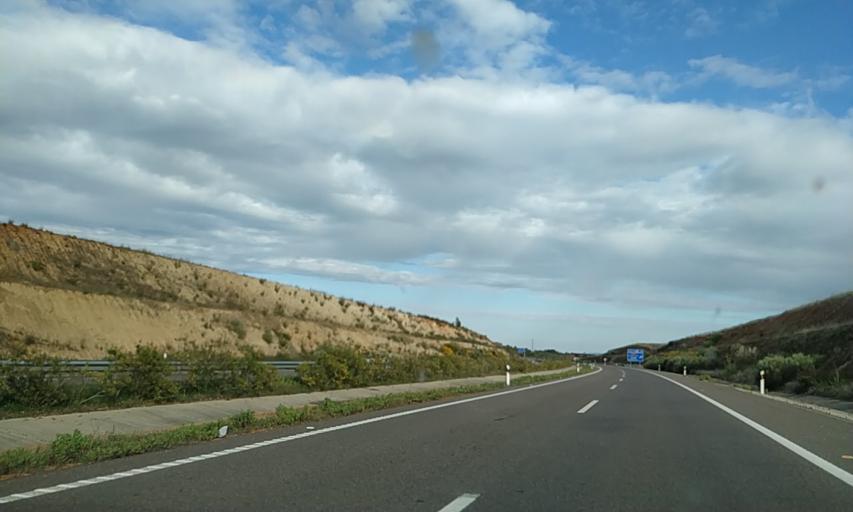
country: ES
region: Extremadura
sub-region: Provincia de Caceres
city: Casas de Don Gomez
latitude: 40.0140
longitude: -6.5815
